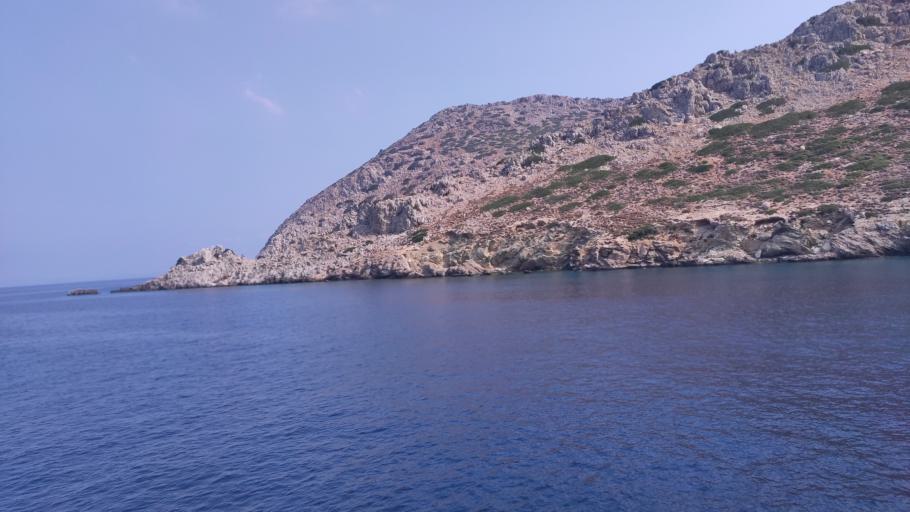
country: GR
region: South Aegean
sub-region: Nomos Dodekanisou
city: Symi
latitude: 36.6449
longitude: 27.8335
